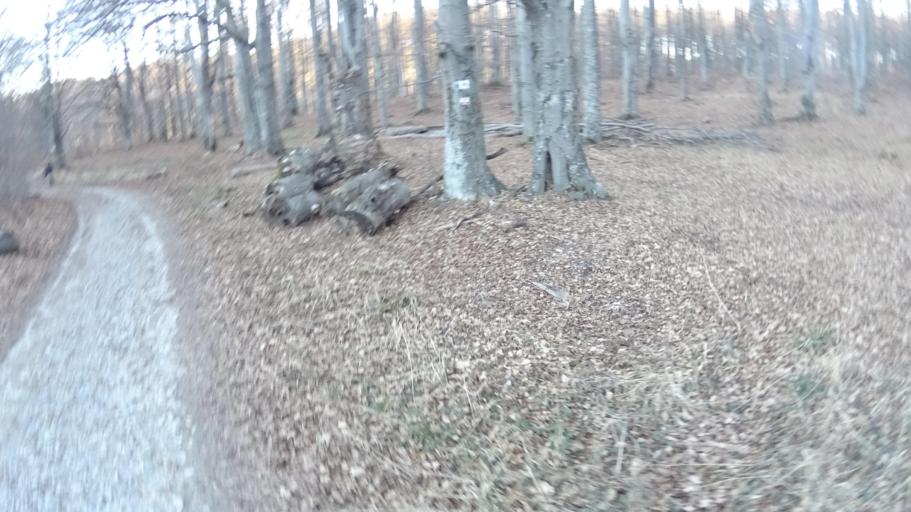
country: HU
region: Heves
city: Szilvasvarad
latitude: 48.0942
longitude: 20.4829
